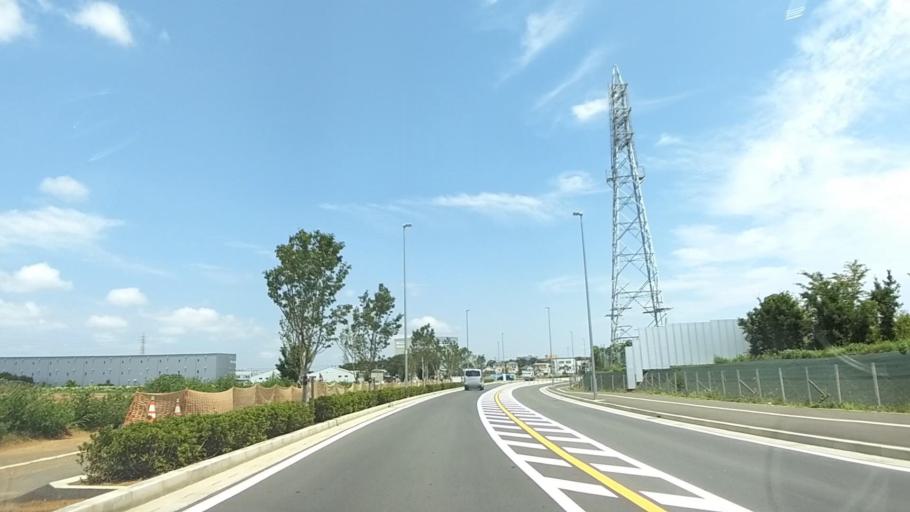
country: JP
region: Kanagawa
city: Minami-rinkan
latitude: 35.4945
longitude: 139.4800
